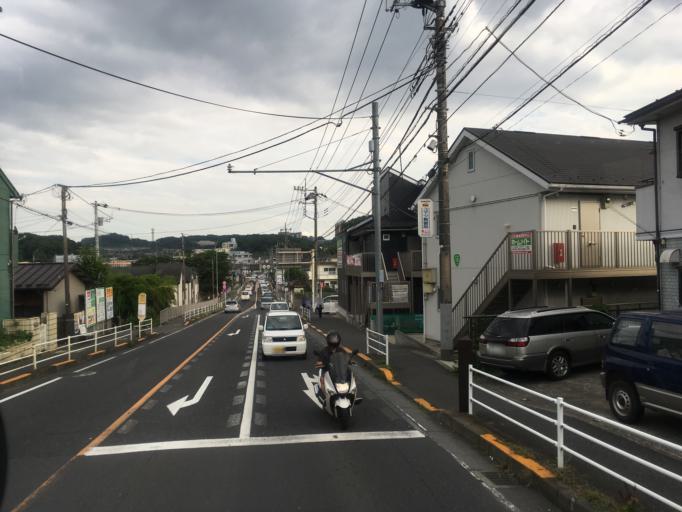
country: JP
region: Tokyo
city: Hachioji
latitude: 35.6427
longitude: 139.3389
